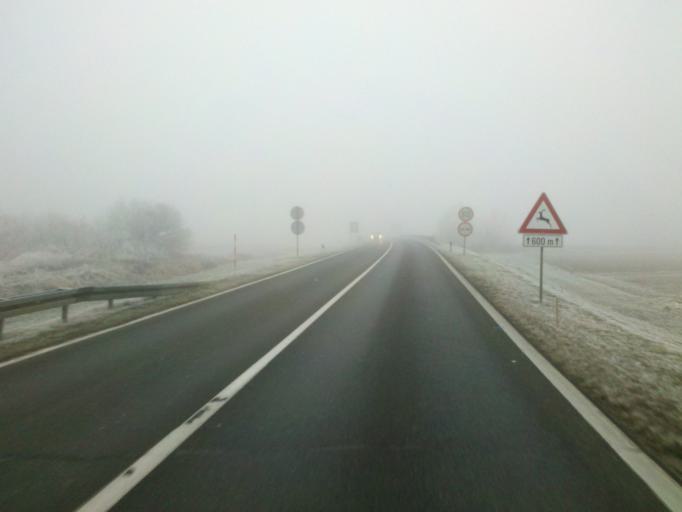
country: HR
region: Medimurska
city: Kursanec
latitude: 46.2631
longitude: 16.3939
